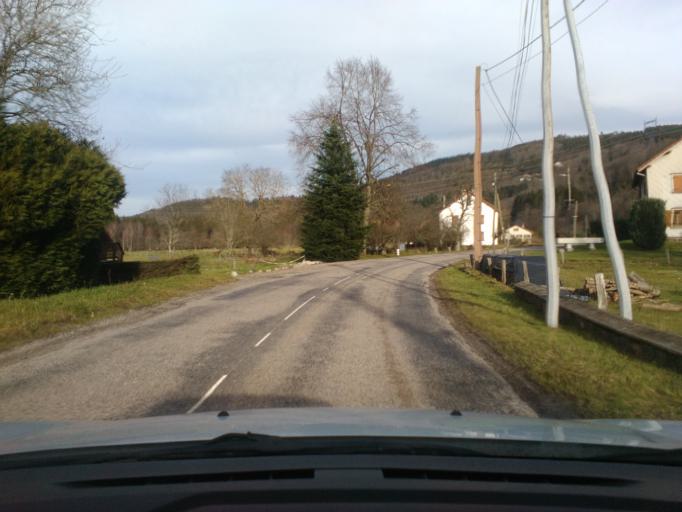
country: FR
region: Lorraine
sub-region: Departement des Vosges
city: Fraize
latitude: 48.1483
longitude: 6.9815
